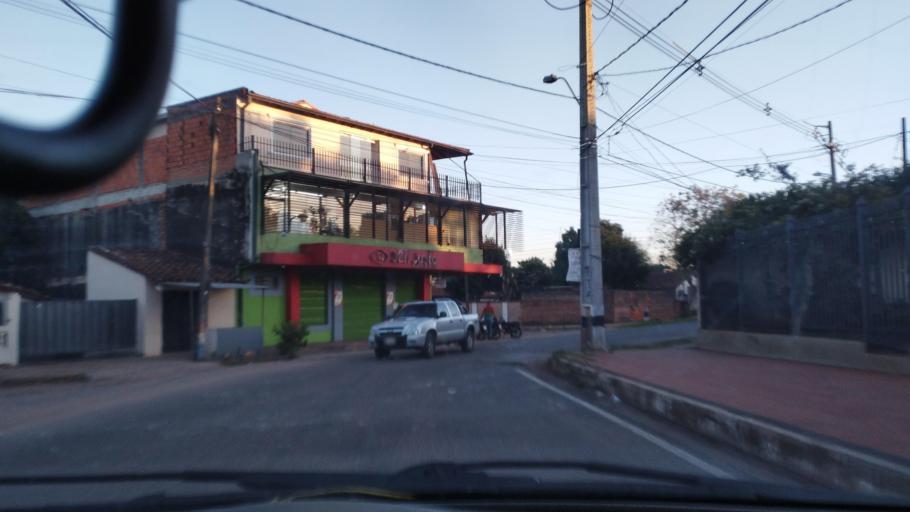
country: PY
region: Central
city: Fernando de la Mora
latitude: -25.3011
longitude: -57.5303
